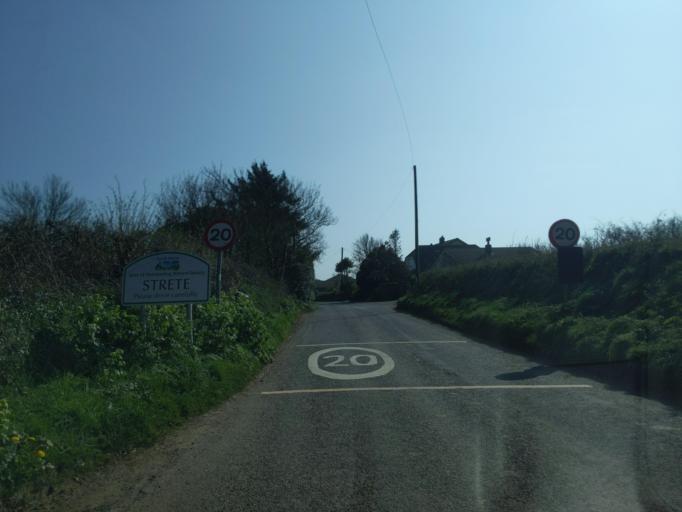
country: GB
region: England
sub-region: Devon
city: Dartmouth
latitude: 50.3141
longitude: -3.6324
